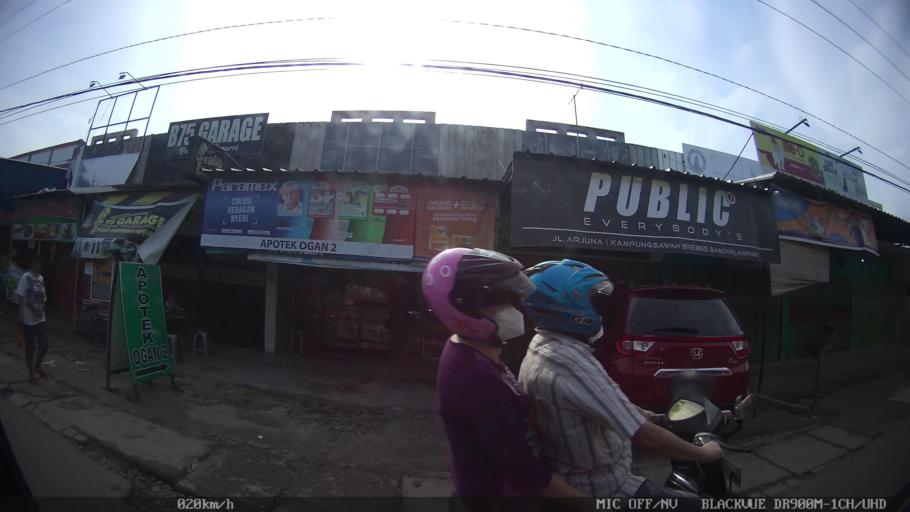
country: ID
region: Lampung
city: Bandarlampung
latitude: -5.4063
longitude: 105.2637
